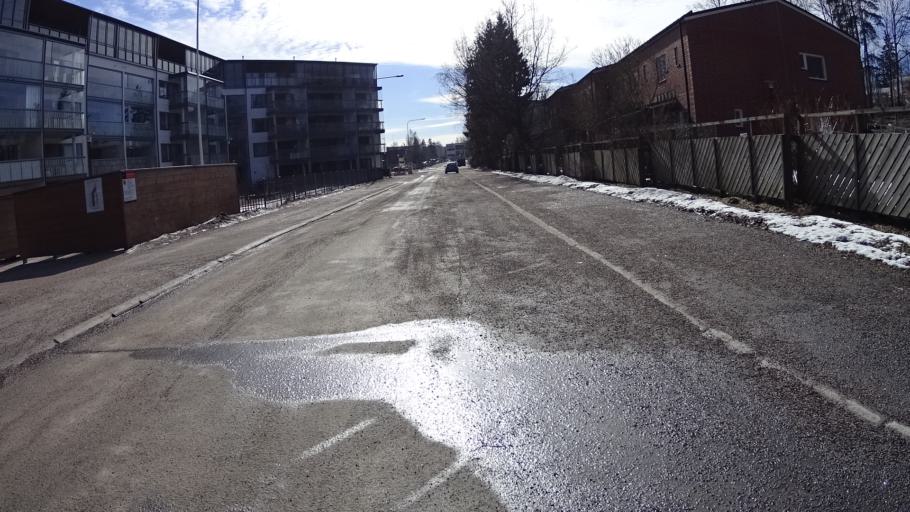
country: FI
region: Uusimaa
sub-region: Helsinki
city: Teekkarikylae
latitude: 60.2287
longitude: 24.8232
